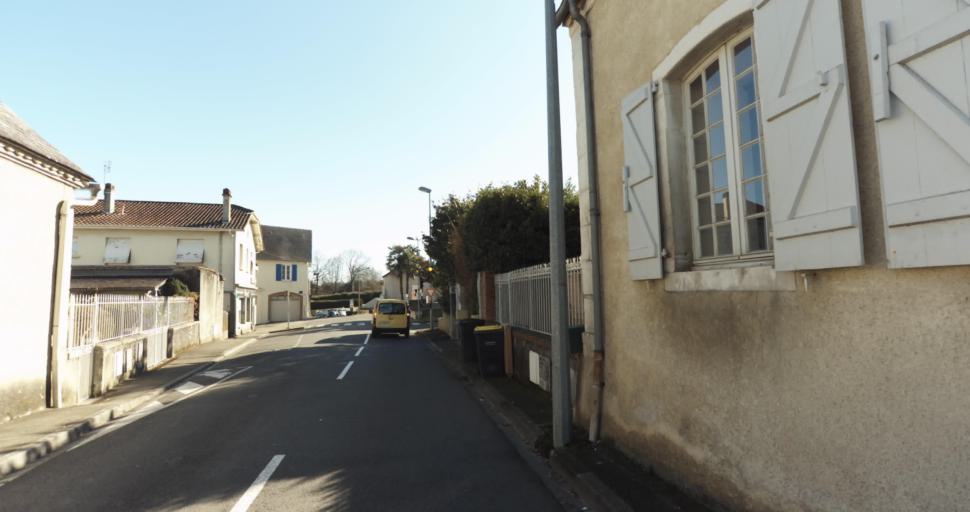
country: FR
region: Aquitaine
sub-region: Departement des Pyrenees-Atlantiques
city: Morlaas
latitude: 43.3478
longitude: -0.2618
